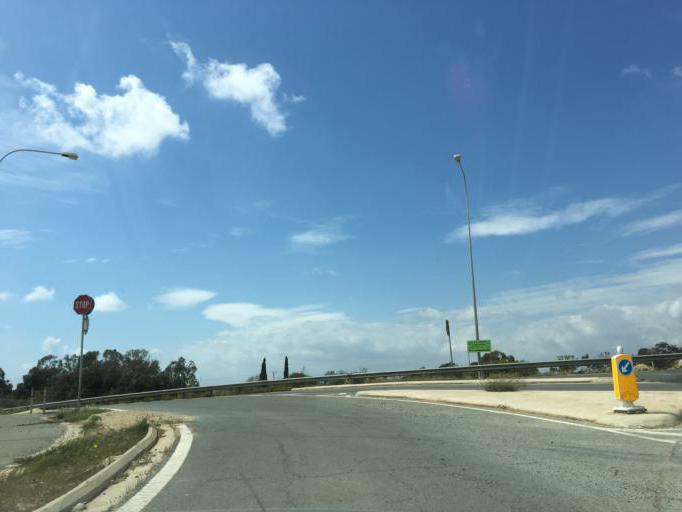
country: CY
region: Ammochostos
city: Liopetri
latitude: 34.9764
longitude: 33.8953
